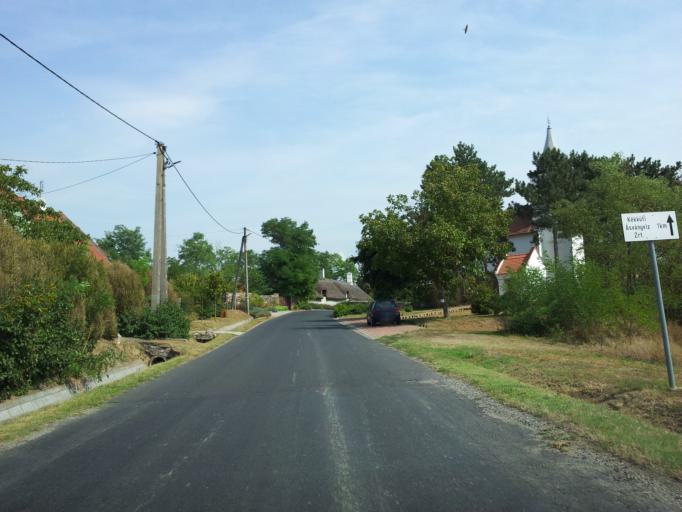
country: HU
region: Veszprem
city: Badacsonytomaj
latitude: 46.8508
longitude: 17.5574
